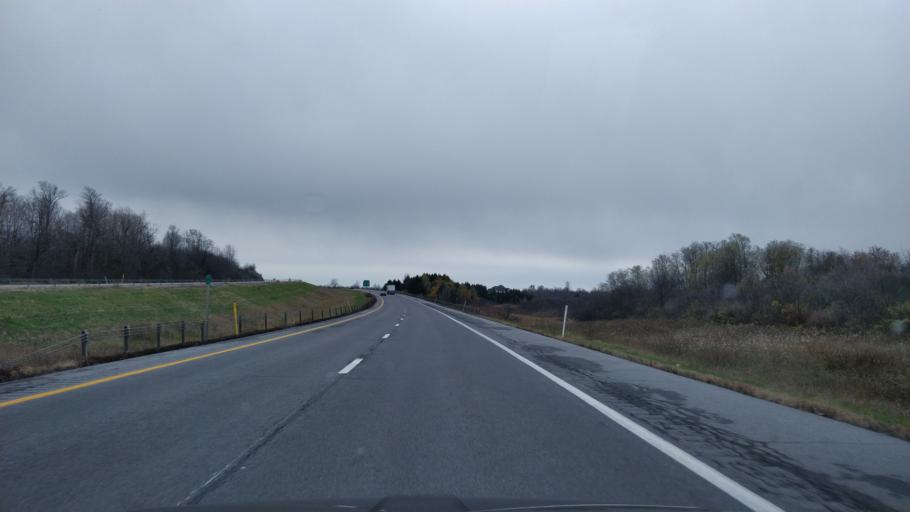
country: US
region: New York
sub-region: Jefferson County
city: Brownville
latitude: 44.0633
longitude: -75.9211
